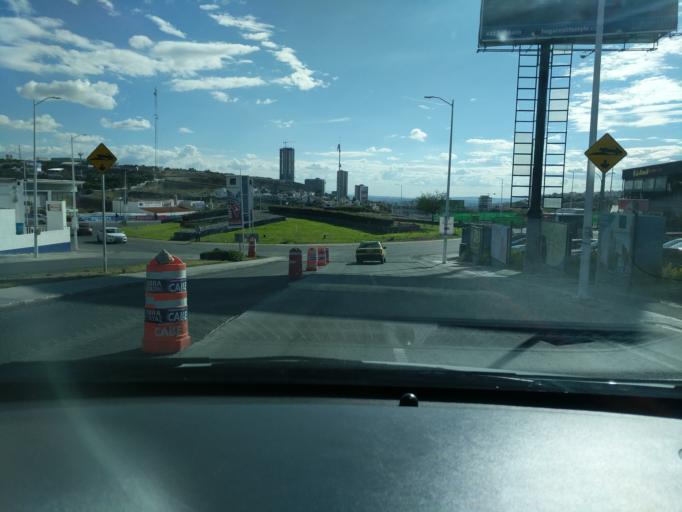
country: MX
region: Queretaro
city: La Canada
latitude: 20.5902
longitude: -100.3369
